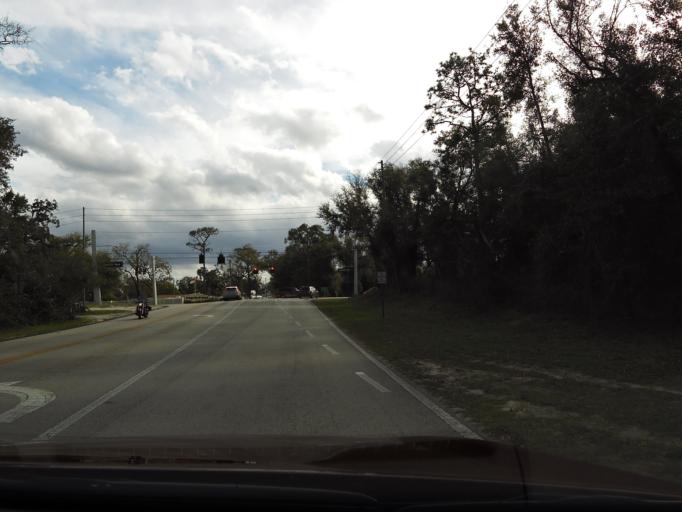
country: US
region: Florida
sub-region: Volusia County
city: Orange City
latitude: 28.9495
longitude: -81.2658
